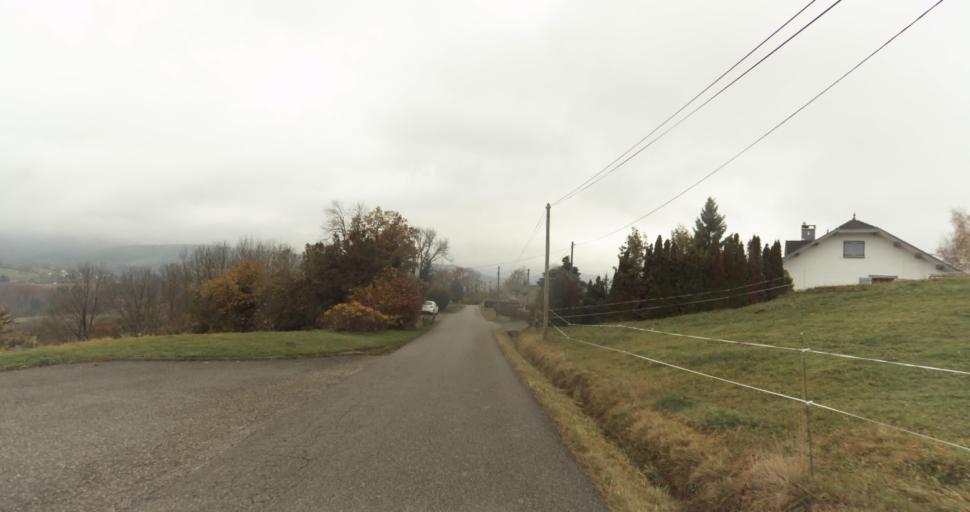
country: FR
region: Rhone-Alpes
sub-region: Departement de la Haute-Savoie
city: Groisy
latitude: 46.0212
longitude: 6.1977
